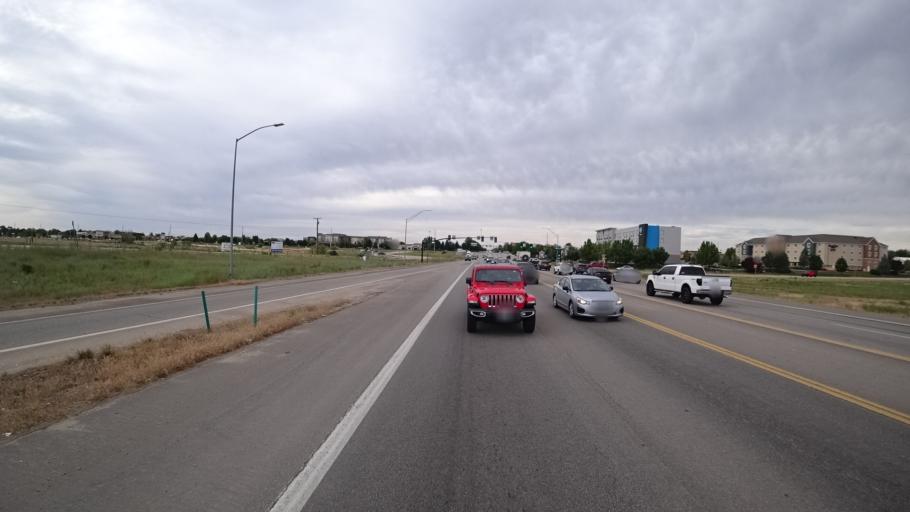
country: US
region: Idaho
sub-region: Ada County
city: Meridian
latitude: 43.5933
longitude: -116.3545
